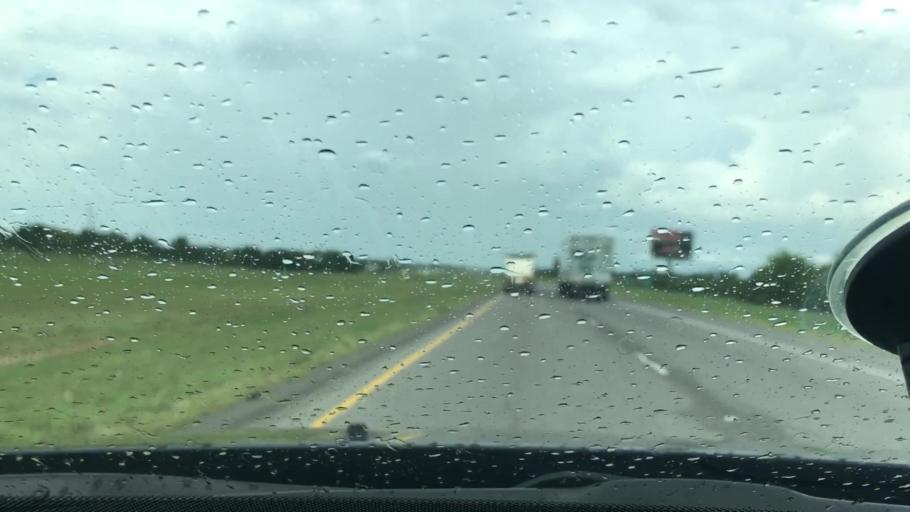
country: US
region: Oklahoma
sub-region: Garvin County
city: Wynnewood
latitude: 34.5593
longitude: -97.1930
